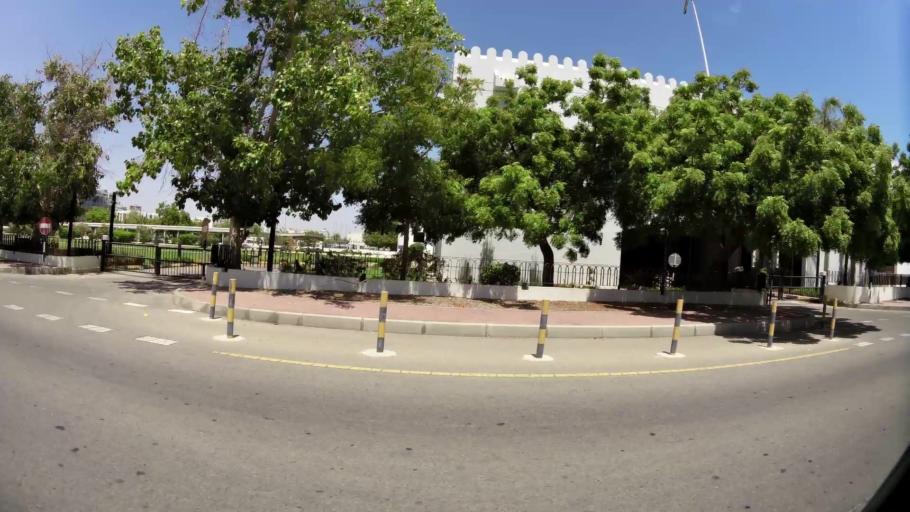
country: OM
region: Muhafazat Masqat
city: Bawshar
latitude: 23.5991
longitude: 58.4364
